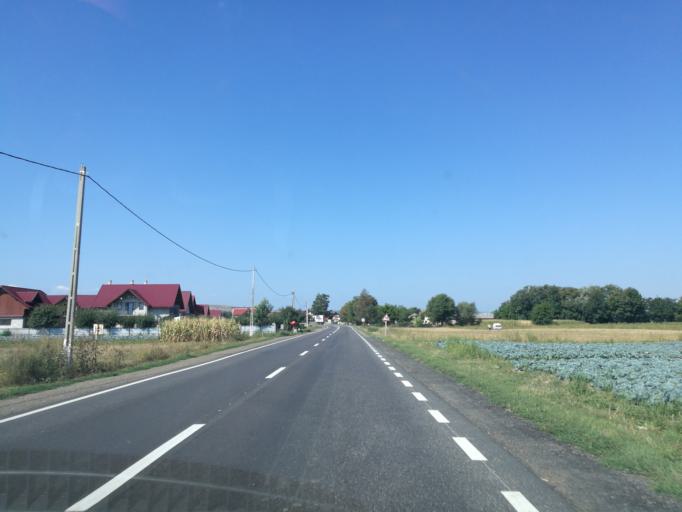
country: RO
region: Suceava
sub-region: Comuna Milisauti
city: Milisauti
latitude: 47.7881
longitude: 26.0190
